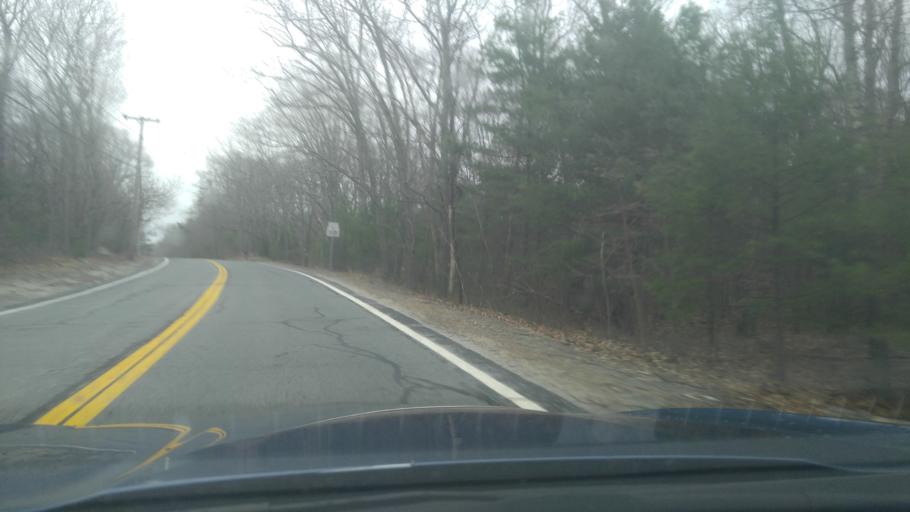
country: US
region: Rhode Island
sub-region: Kent County
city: Coventry
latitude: 41.6794
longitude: -71.6597
